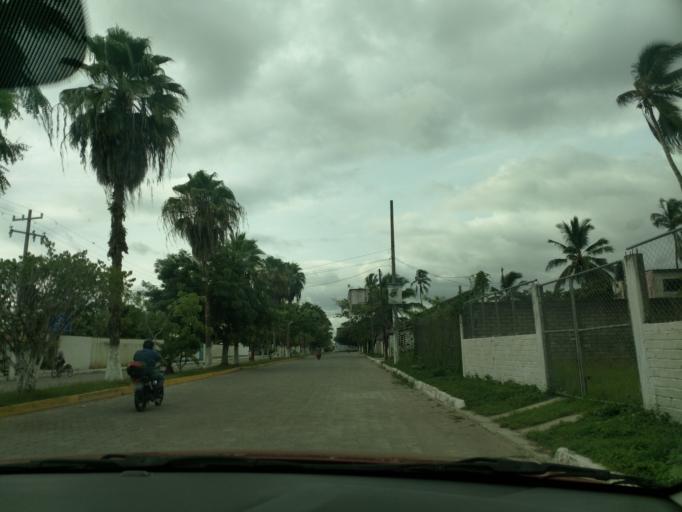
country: MX
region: Nayarit
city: San Blas
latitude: 21.5342
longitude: -105.2838
